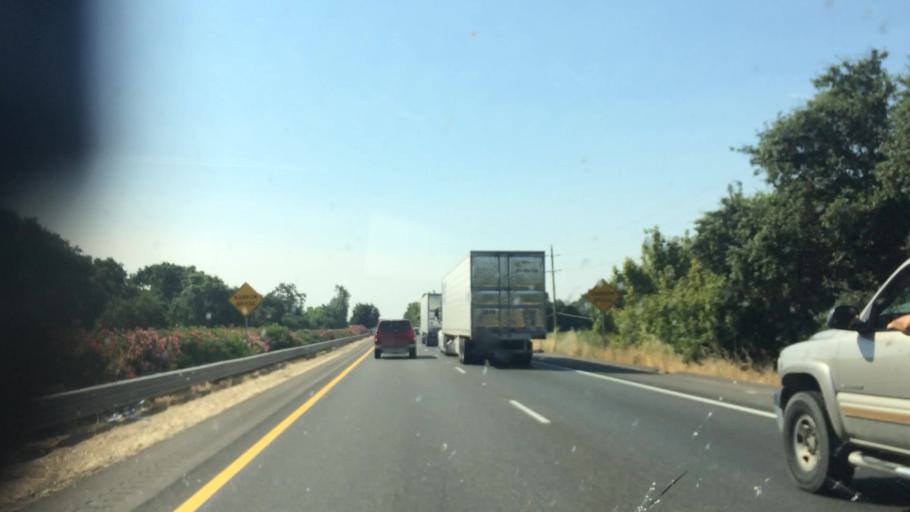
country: US
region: California
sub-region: Sacramento County
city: Elk Grove
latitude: 38.3544
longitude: -121.3418
